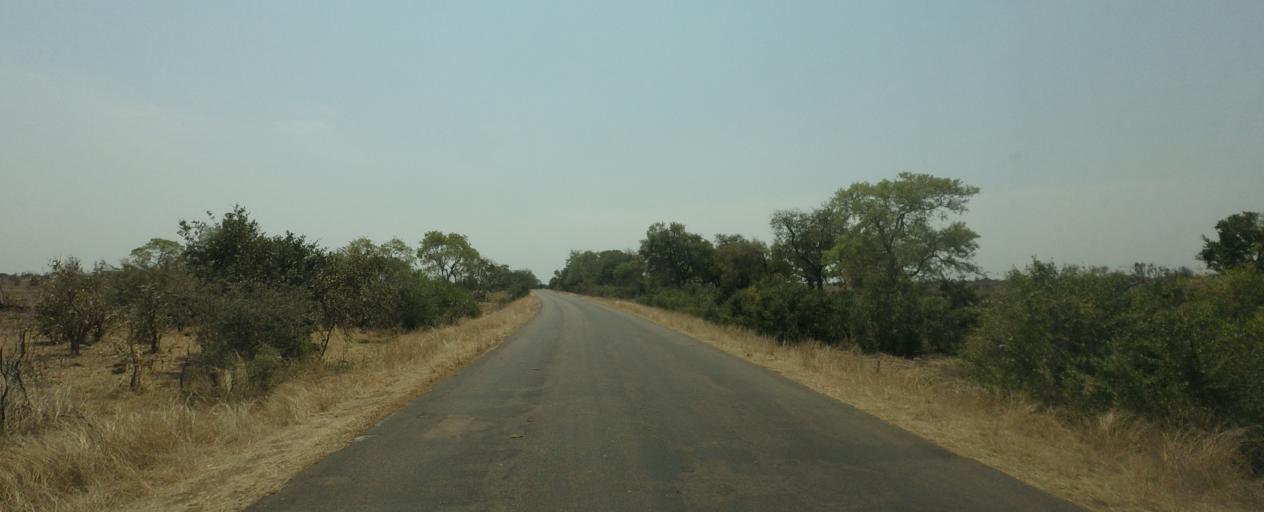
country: ZA
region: Limpopo
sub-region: Mopani District Municipality
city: Phalaborwa
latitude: -24.1637
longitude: 31.7202
